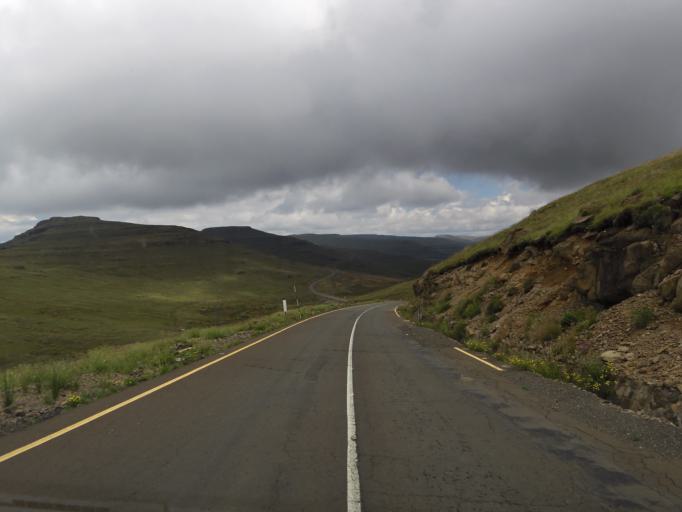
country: LS
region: Butha-Buthe
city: Butha-Buthe
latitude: -29.0735
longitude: 28.4253
